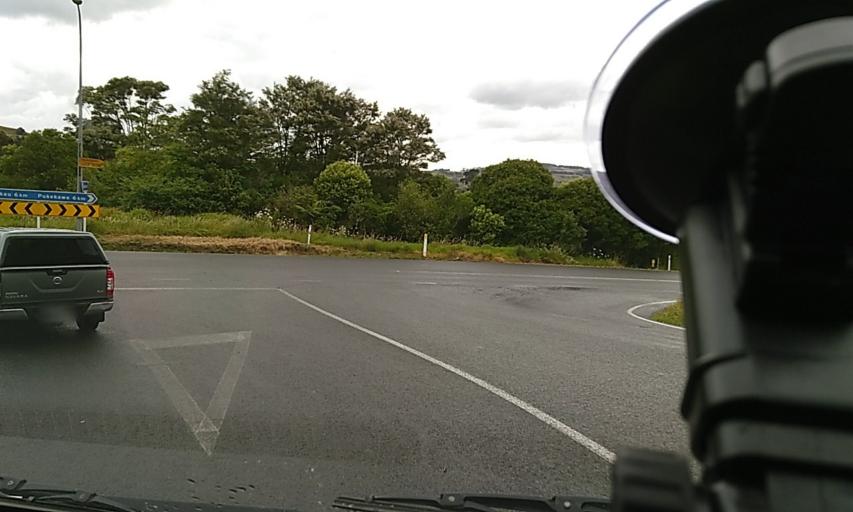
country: NZ
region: Auckland
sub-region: Auckland
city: Pukekohe East
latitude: -37.2996
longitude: 174.9443
